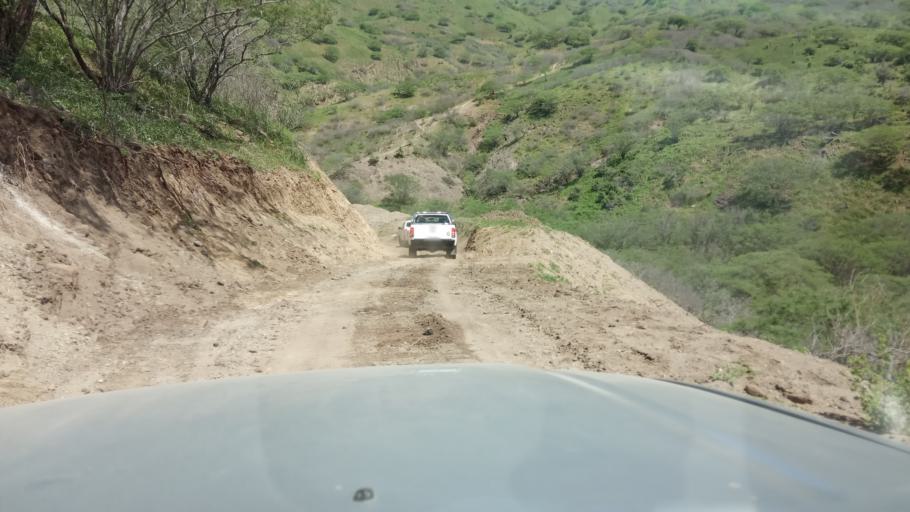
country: CV
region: Santa Catarina
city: Assomada
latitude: 15.1139
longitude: -23.7287
